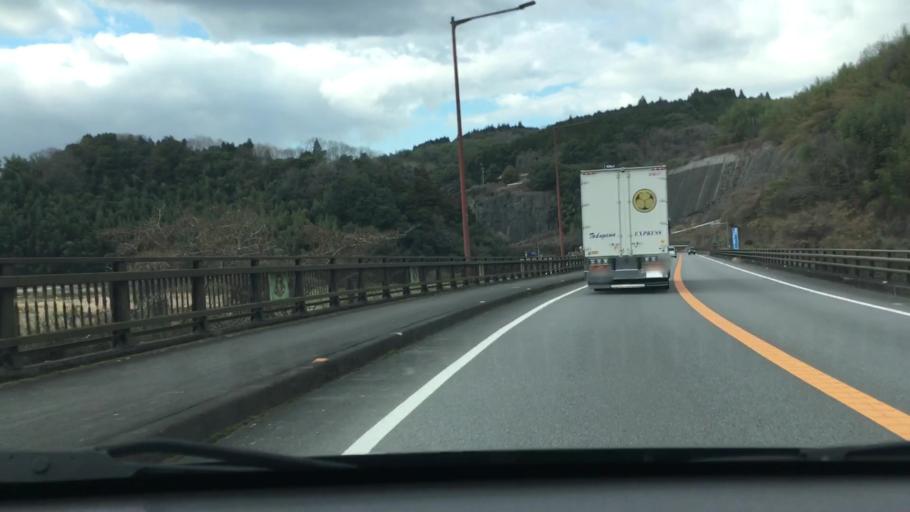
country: JP
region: Oita
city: Usuki
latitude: 33.0666
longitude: 131.6564
